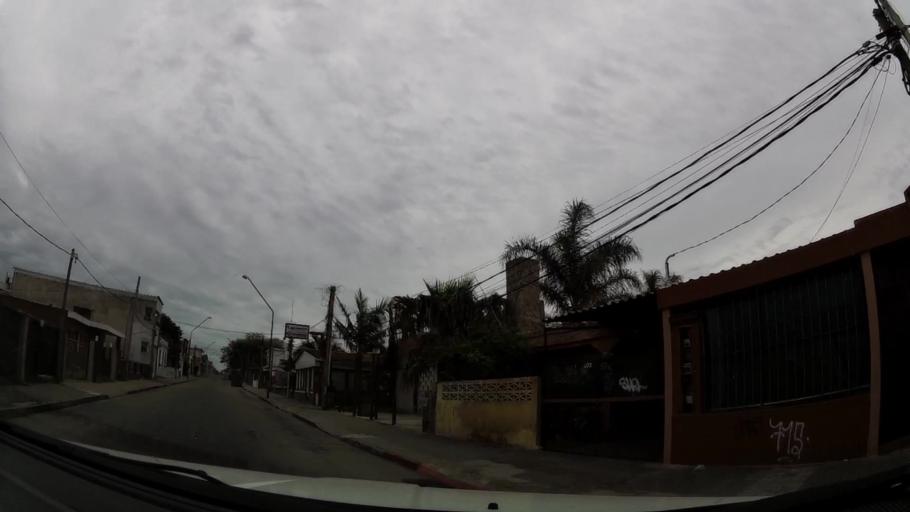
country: UY
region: Maldonado
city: Maldonado
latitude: -34.9046
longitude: -54.9545
